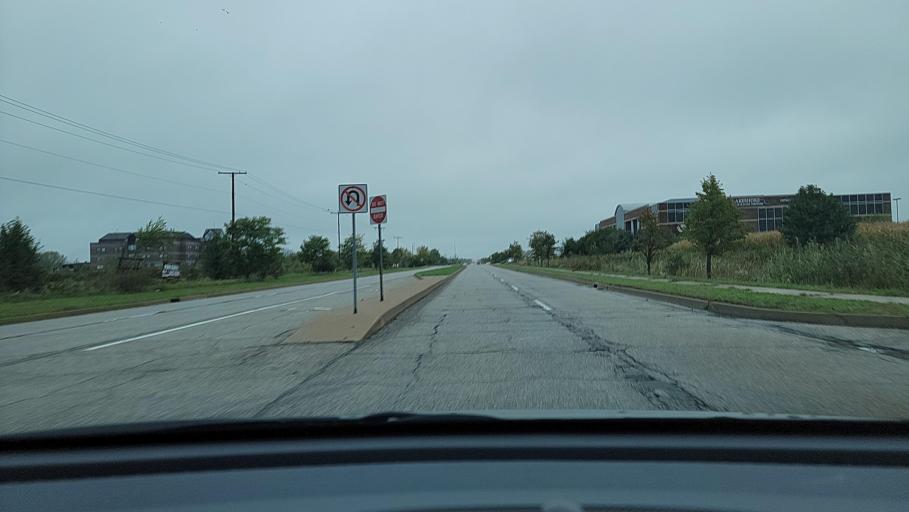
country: US
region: Indiana
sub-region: Porter County
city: Portage
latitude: 41.5434
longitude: -87.1824
